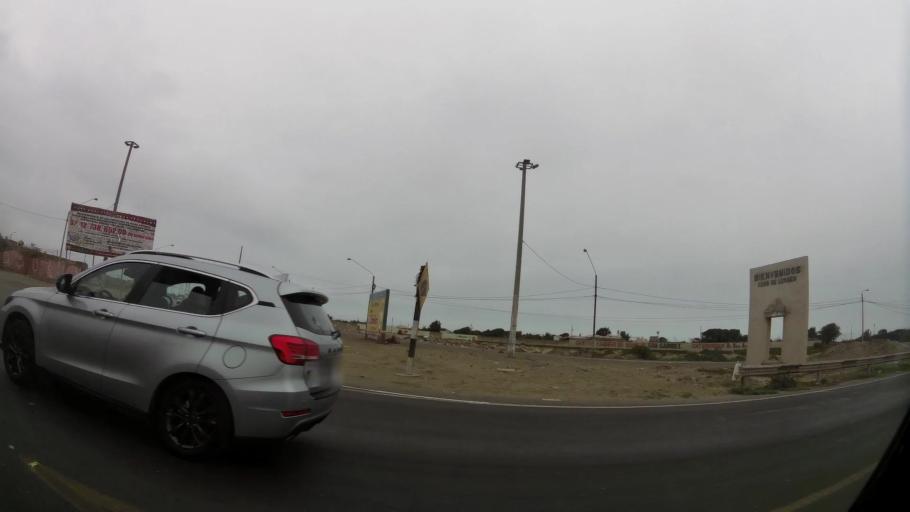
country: PE
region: La Libertad
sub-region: Provincia de Trujillo
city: Moche
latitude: -8.1750
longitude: -78.9968
